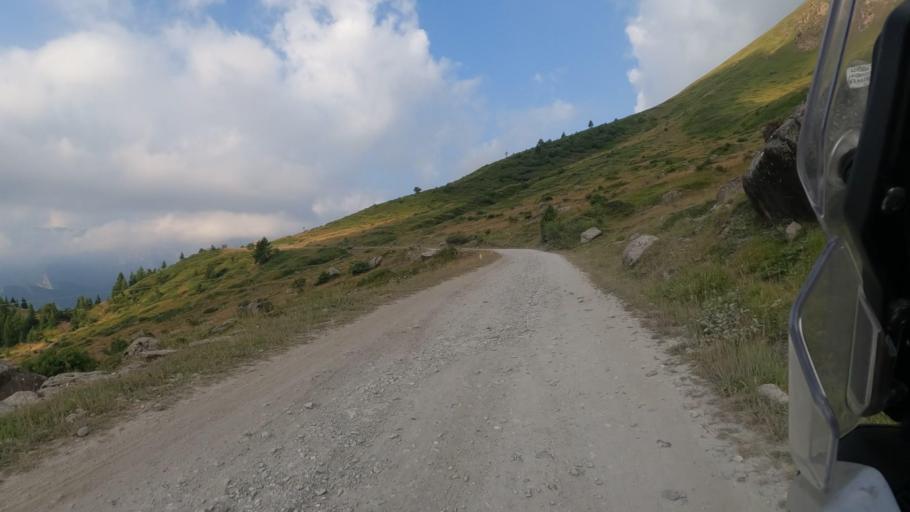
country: IT
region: Piedmont
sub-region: Provincia di Torino
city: Usseaux
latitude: 45.0666
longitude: 7.0311
